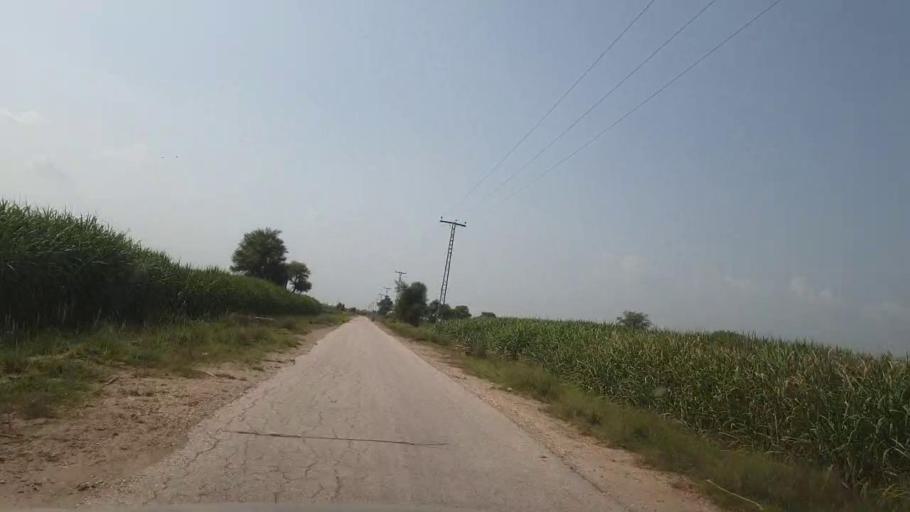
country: PK
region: Sindh
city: Pano Aqil
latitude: 27.7854
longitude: 69.1577
